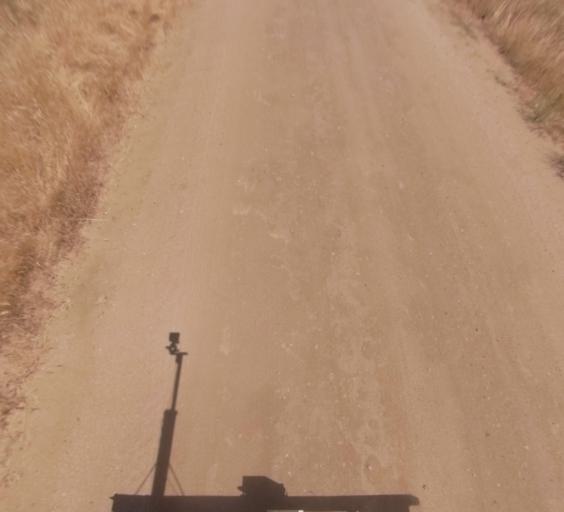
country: US
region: California
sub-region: Madera County
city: Madera Acres
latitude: 37.1139
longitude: -120.0203
